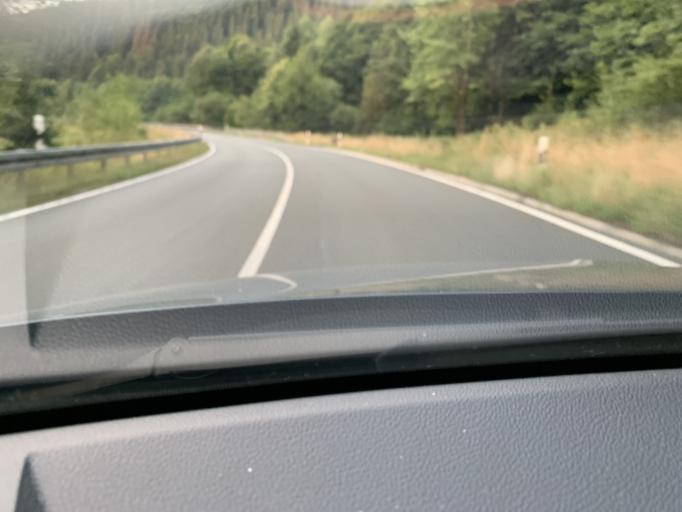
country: DE
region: Thuringia
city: Judenbach
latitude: 50.4037
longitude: 11.1891
